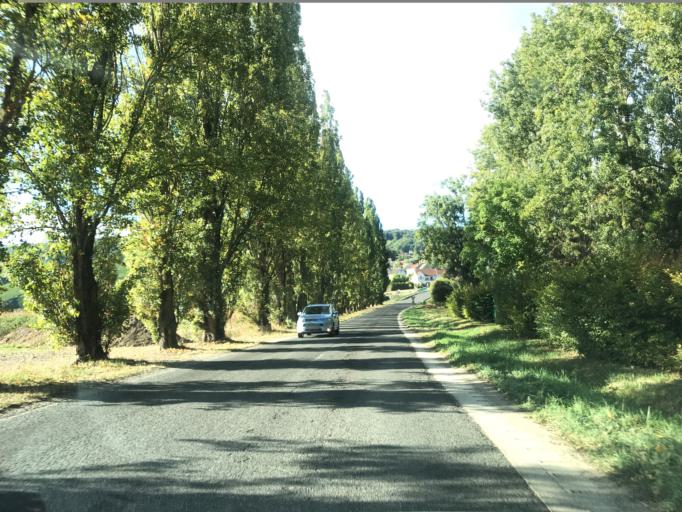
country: FR
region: Champagne-Ardenne
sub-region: Departement de la Marne
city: Mareuil-le-Port
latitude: 49.0794
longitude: 3.7963
